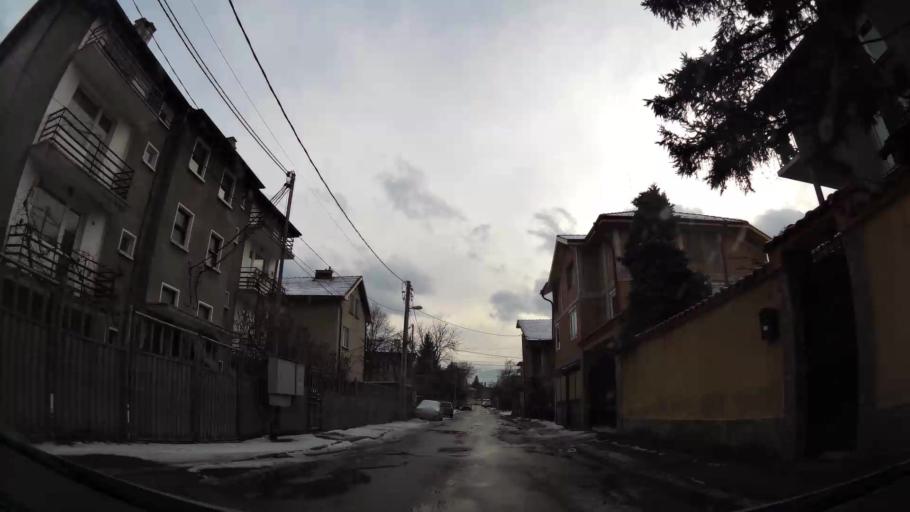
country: BG
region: Sofia-Capital
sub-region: Stolichna Obshtina
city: Sofia
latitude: 42.7245
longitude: 23.3318
